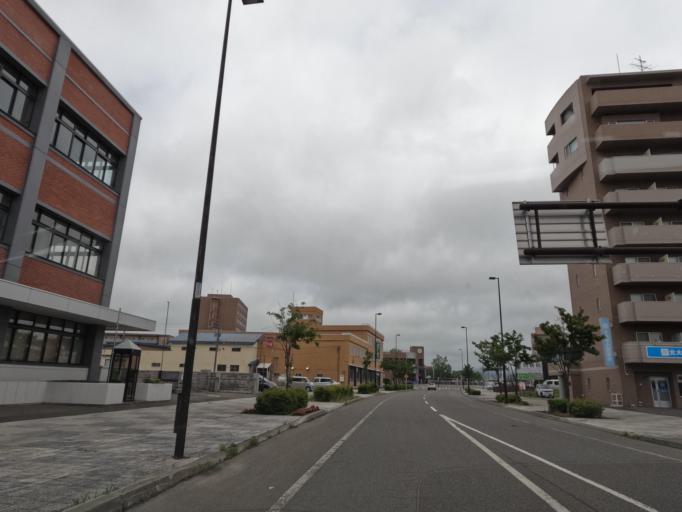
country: JP
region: Hokkaido
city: Tobetsu
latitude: 43.2205
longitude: 141.5150
